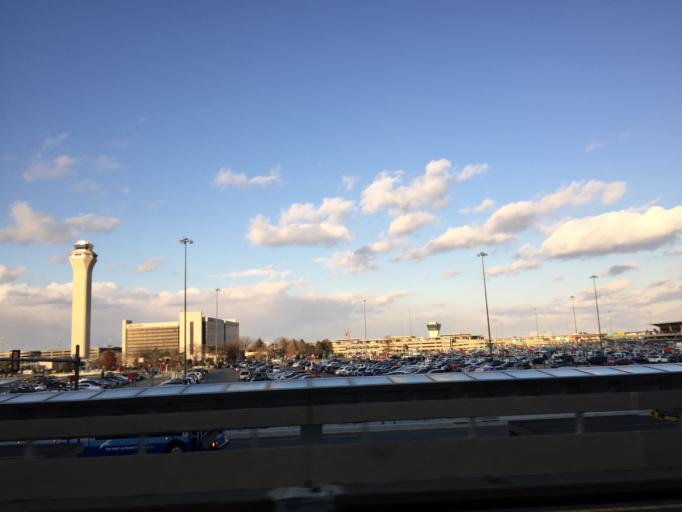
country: US
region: New Jersey
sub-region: Union County
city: Elizabeth
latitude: 40.6880
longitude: -74.1827
